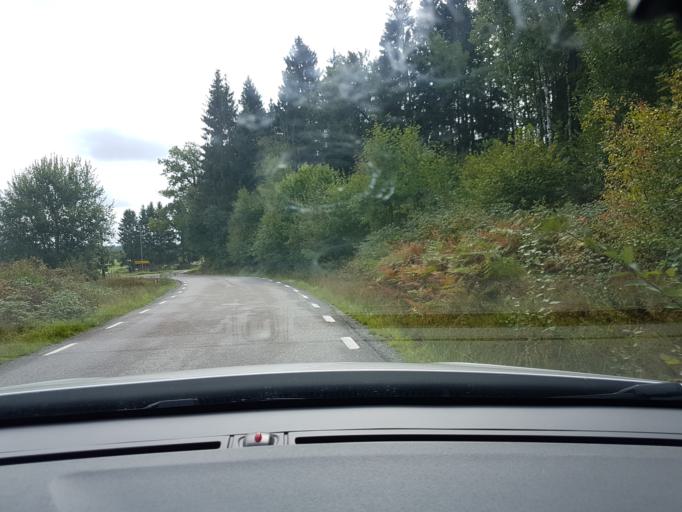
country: SE
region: Vaestra Goetaland
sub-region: Ale Kommun
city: Alvangen
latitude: 57.9193
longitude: 12.1331
